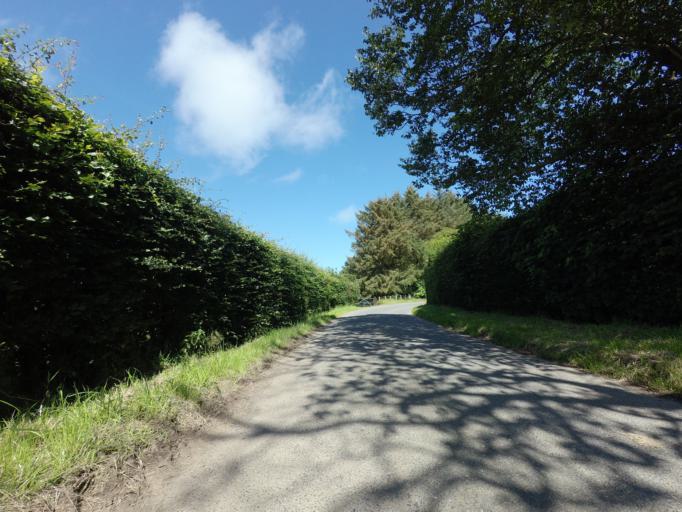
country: GB
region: Scotland
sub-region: Aberdeenshire
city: Banff
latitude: 57.6166
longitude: -2.5090
